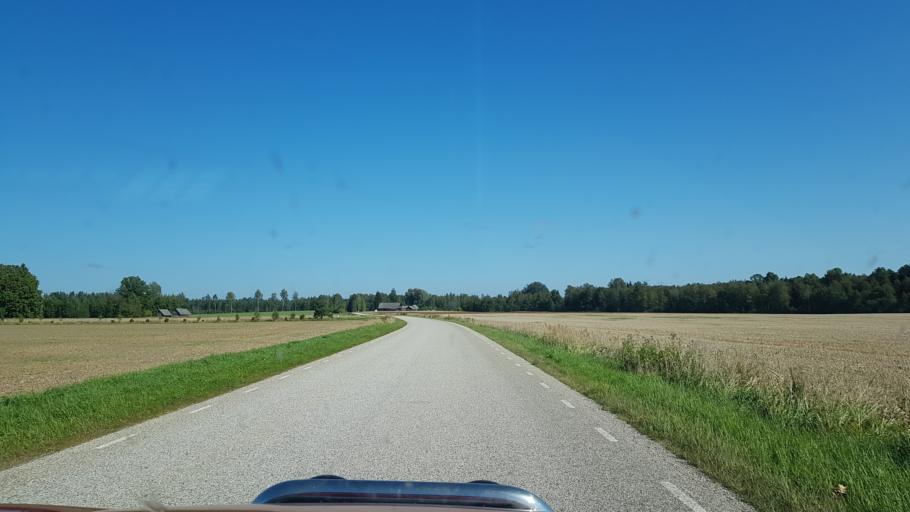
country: EE
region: Polvamaa
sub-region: Raepina vald
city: Rapina
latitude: 58.2132
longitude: 27.2704
